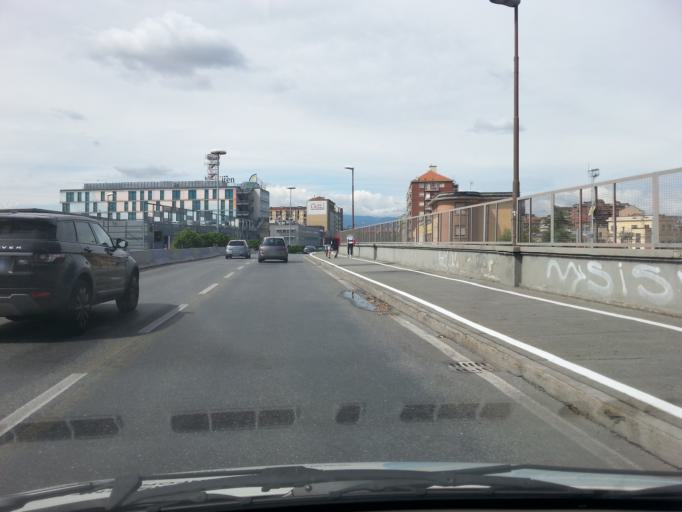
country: IT
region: Piedmont
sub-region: Provincia di Torino
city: Turin
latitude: 45.0437
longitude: 7.6675
